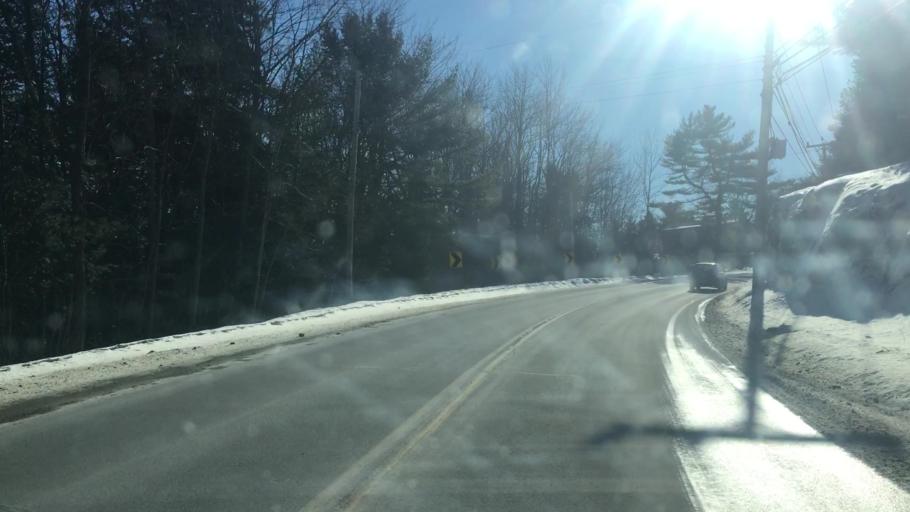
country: US
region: Maine
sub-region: Hancock County
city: Ellsworth
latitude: 44.5206
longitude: -68.4309
